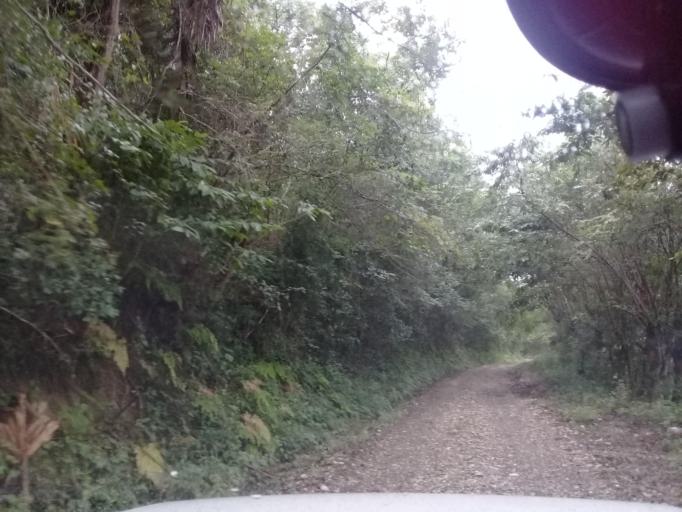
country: MX
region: Veracruz
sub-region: Chalma
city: San Pedro Coyutla
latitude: 21.2470
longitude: -98.4146
